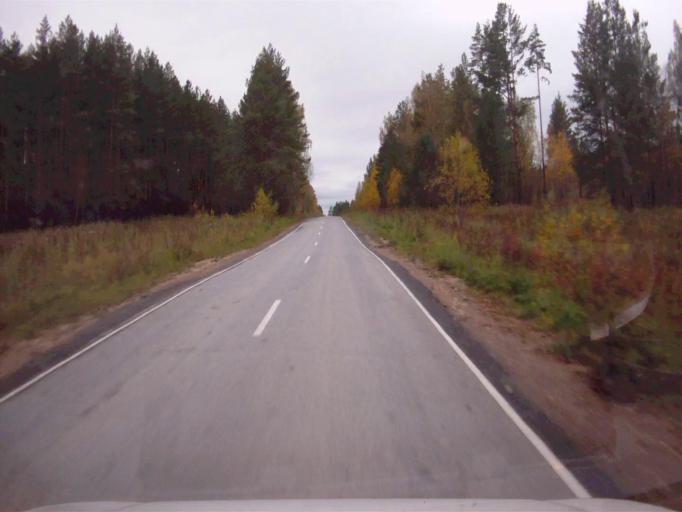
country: RU
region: Chelyabinsk
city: Nyazepetrovsk
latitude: 56.0543
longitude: 59.4776
